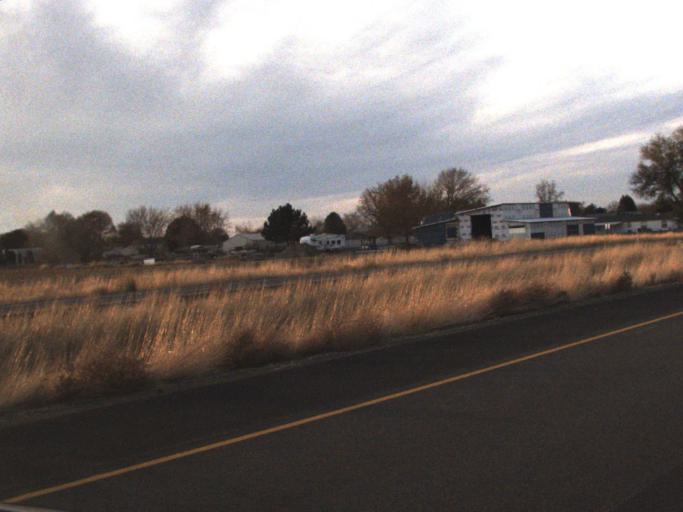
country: US
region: Washington
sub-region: Walla Walla County
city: Burbank
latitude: 46.1935
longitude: -118.9901
